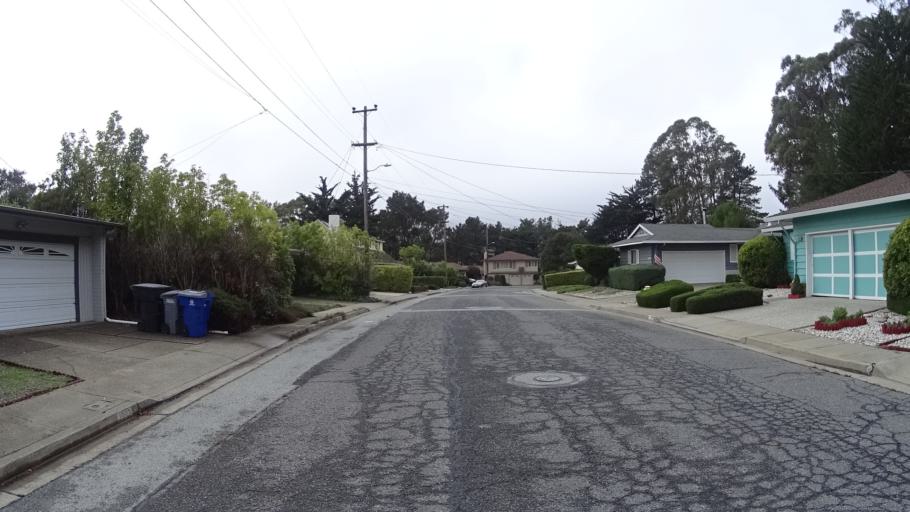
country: US
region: California
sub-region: San Mateo County
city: San Bruno
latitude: 37.6073
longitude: -122.4218
